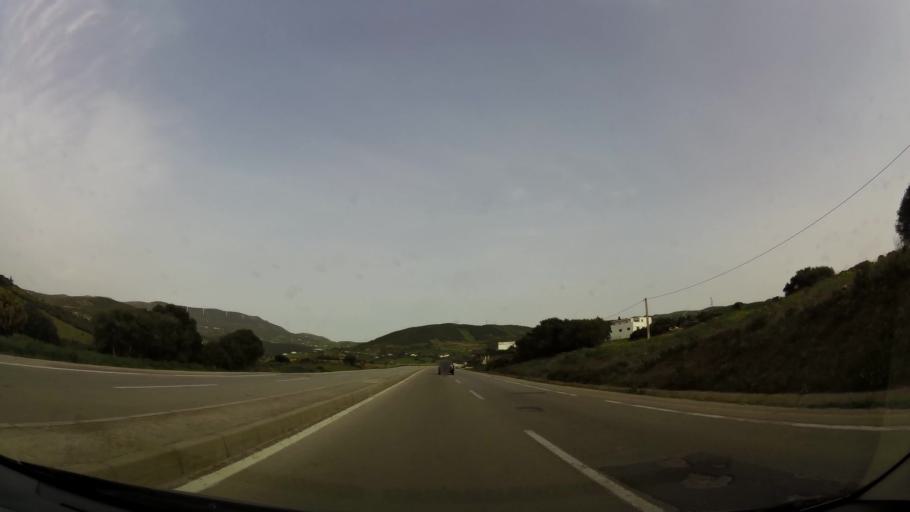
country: MA
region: Tanger-Tetouan
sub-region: Tanger-Assilah
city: Dar Chaoui
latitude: 35.5677
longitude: -5.6100
